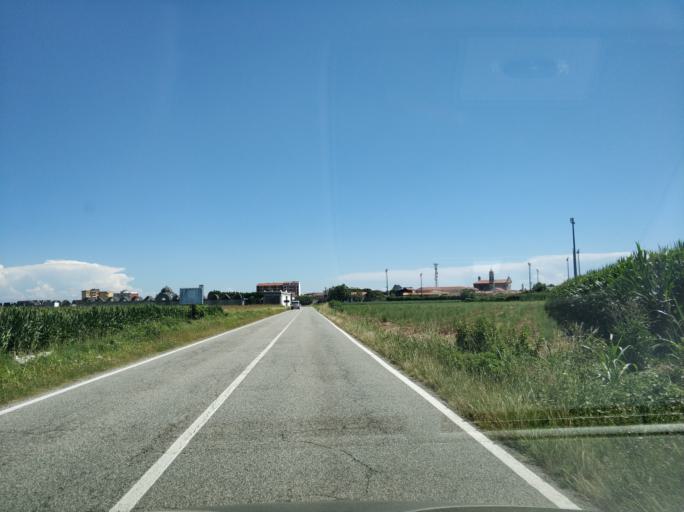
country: IT
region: Piedmont
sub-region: Provincia di Vercelli
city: Cigliano
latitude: 45.3162
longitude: 8.0198
